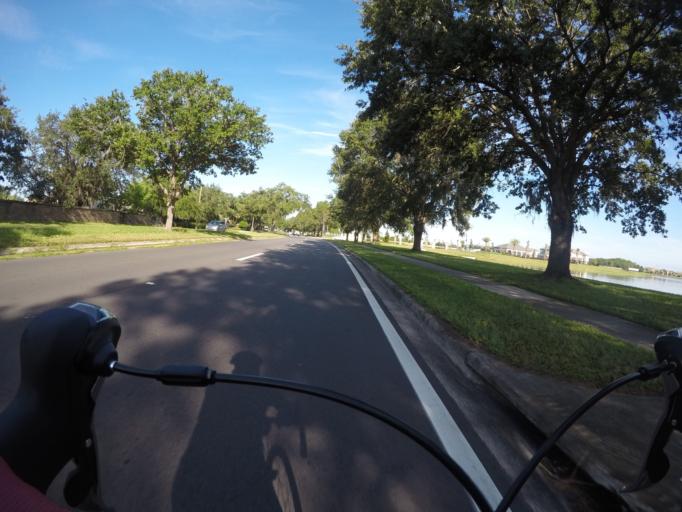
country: US
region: Florida
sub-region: Orange County
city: Meadow Woods
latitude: 28.3620
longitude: -81.3599
